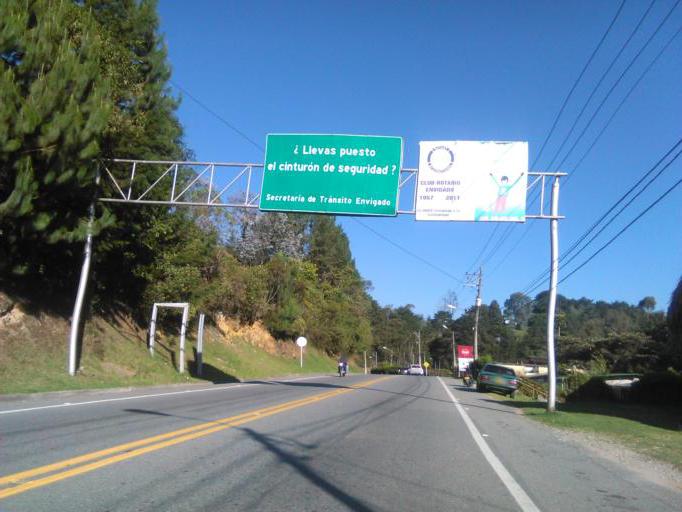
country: CO
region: Antioquia
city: Envigado
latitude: 6.1483
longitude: -75.5284
